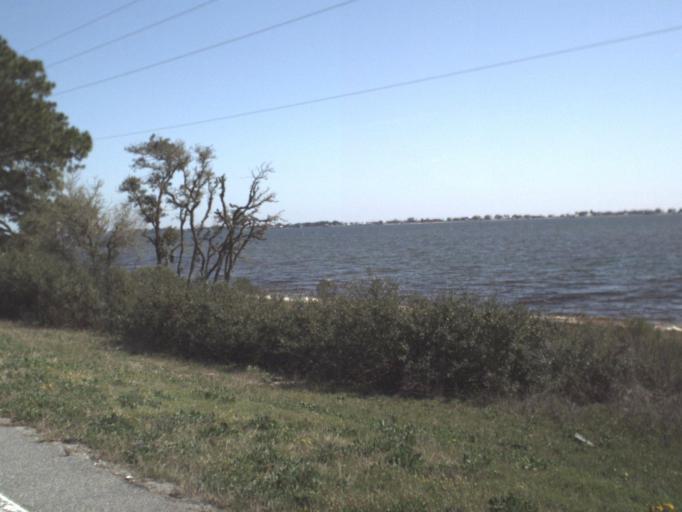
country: US
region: Florida
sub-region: Wakulla County
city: Crawfordville
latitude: 29.9242
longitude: -84.4148
